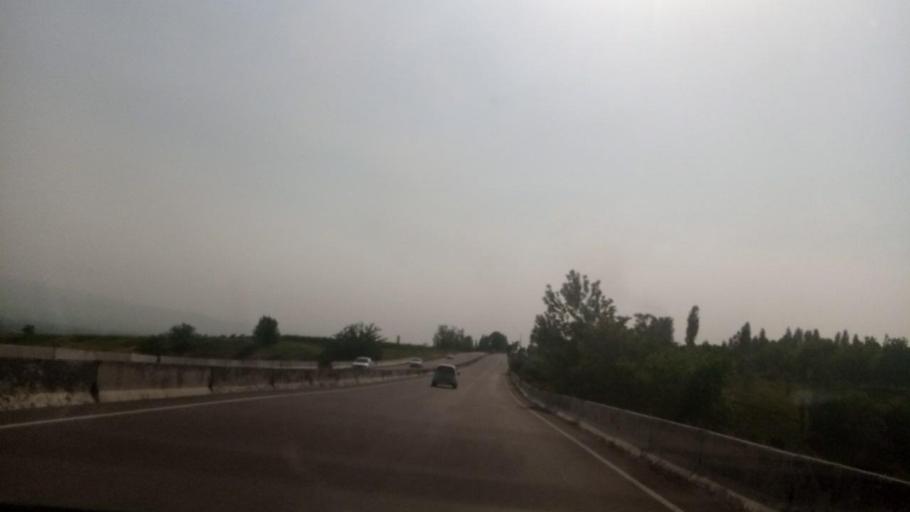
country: UZ
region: Toshkent
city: Angren
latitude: 40.9397
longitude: 69.9014
